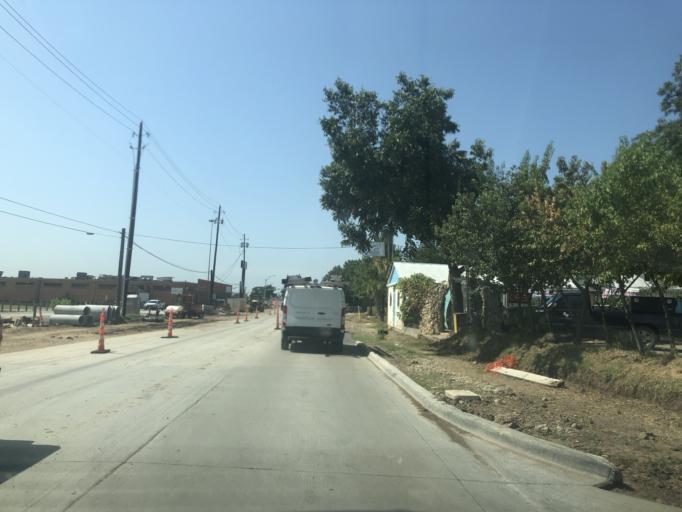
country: US
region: Texas
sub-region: Tarrant County
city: Westworth
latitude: 32.7353
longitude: -97.3701
